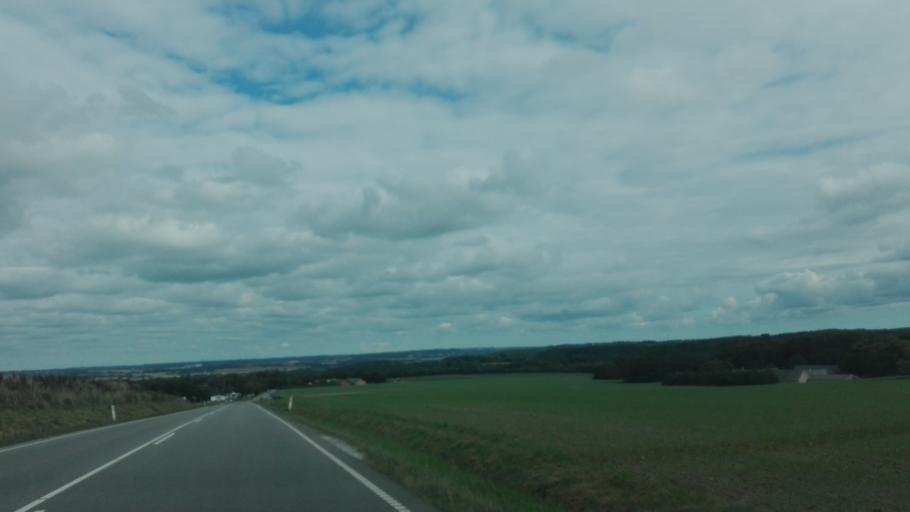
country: DK
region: Central Jutland
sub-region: Skanderborg Kommune
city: Stilling
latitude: 56.1075
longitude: 9.9746
